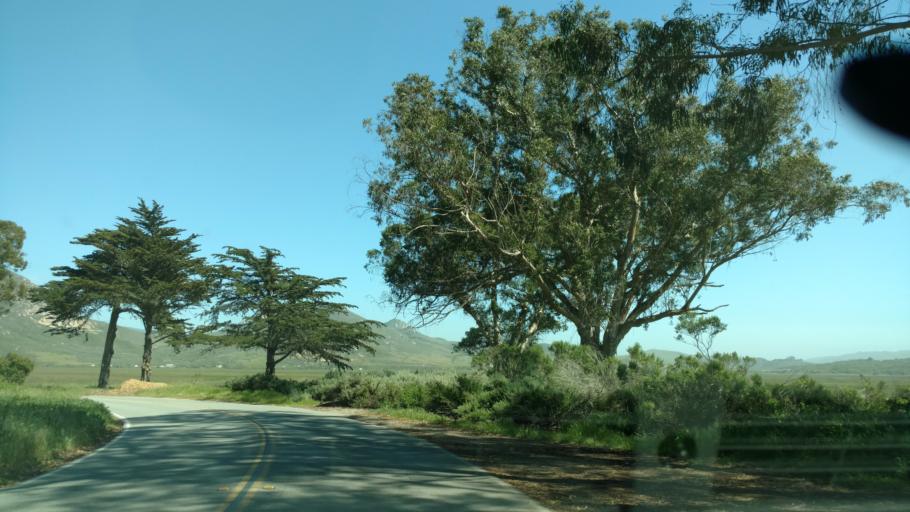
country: US
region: California
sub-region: San Luis Obispo County
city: Morro Bay
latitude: 35.3456
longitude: -120.8394
